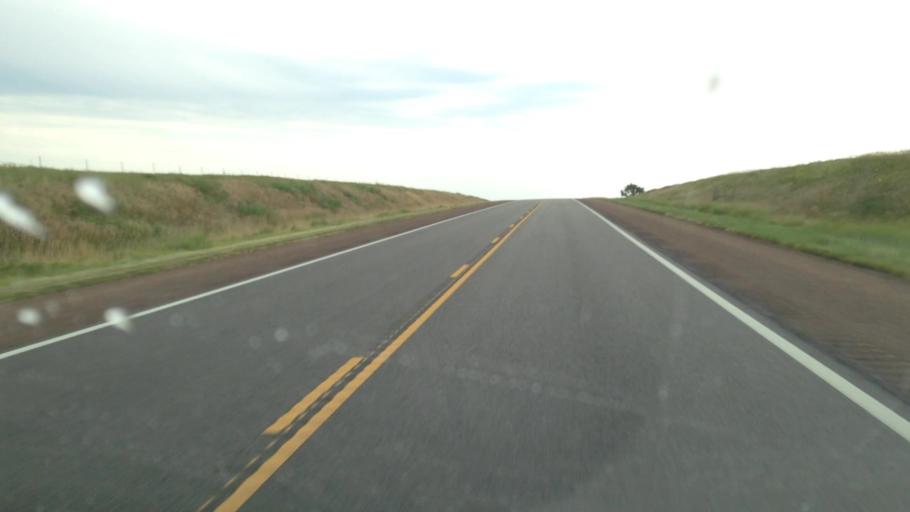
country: US
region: Kansas
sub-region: Coffey County
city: Burlington
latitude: 38.0492
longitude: -95.7391
